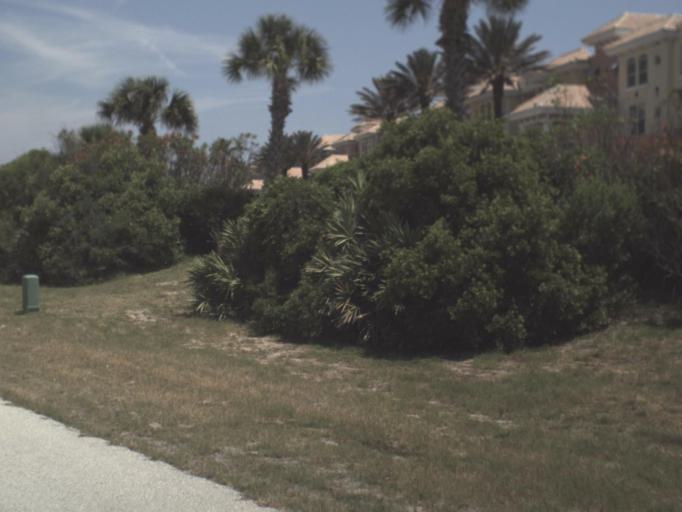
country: US
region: Florida
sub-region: Saint Johns County
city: Villano Beach
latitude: 29.9665
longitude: -81.3094
